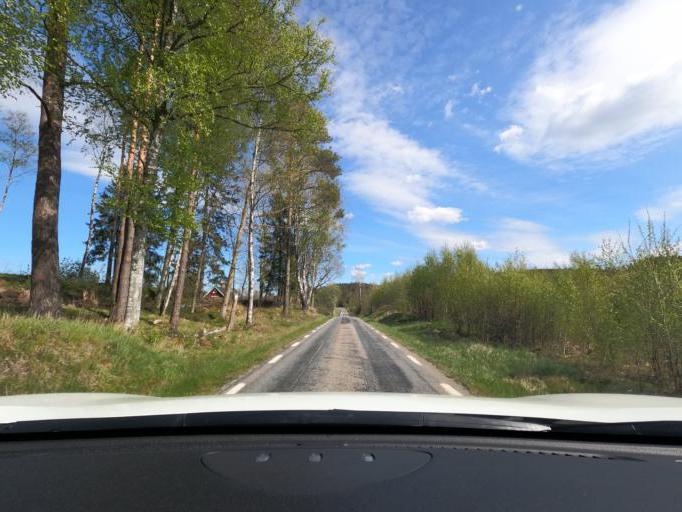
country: SE
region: Vaestra Goetaland
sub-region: Marks Kommun
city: Horred
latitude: 57.4507
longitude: 12.4549
